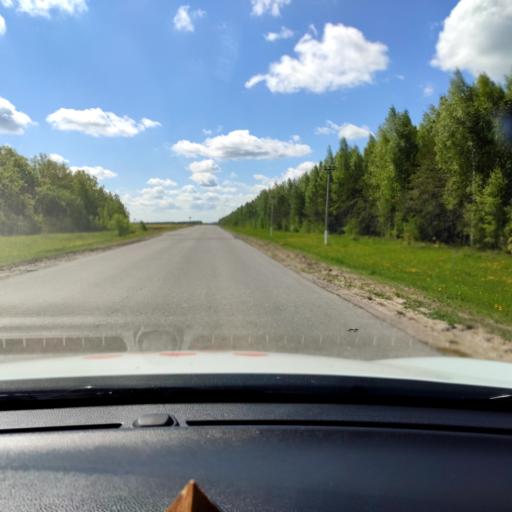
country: RU
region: Tatarstan
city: Verkhniy Uslon
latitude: 55.6168
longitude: 48.8788
